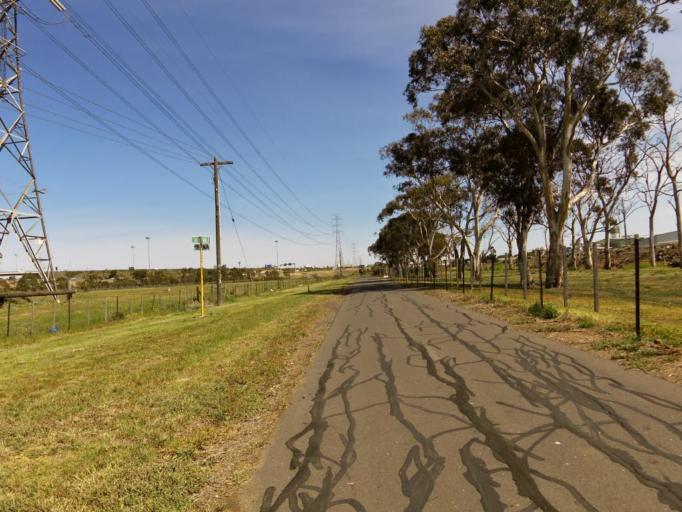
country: AU
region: Victoria
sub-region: Brimbank
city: Brooklyn
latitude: -37.8236
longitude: 144.8192
